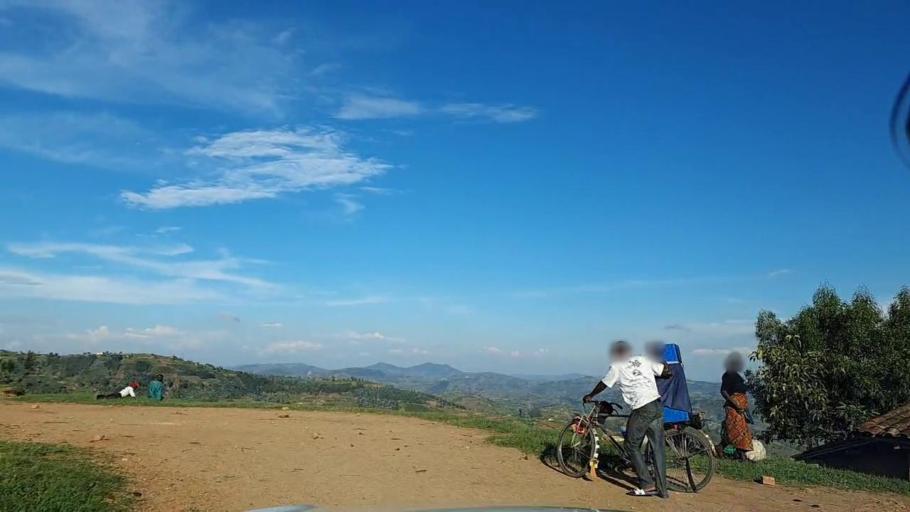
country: RW
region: Southern Province
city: Gikongoro
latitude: -2.4140
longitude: 29.5186
